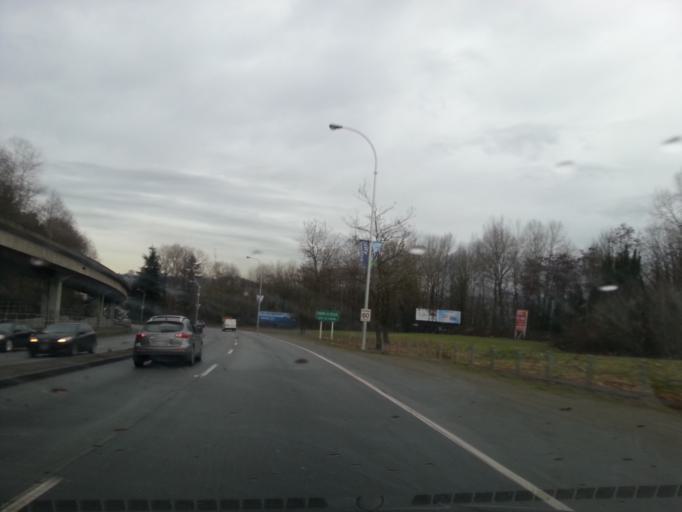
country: CA
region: British Columbia
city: New Westminster
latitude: 49.2071
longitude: -122.8581
